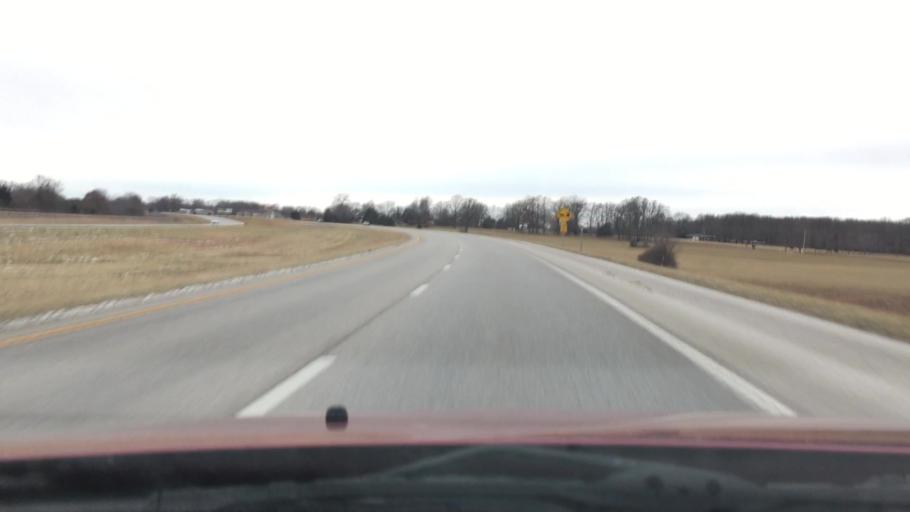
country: US
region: Missouri
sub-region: Webster County
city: Seymour
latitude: 37.1675
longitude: -92.8044
